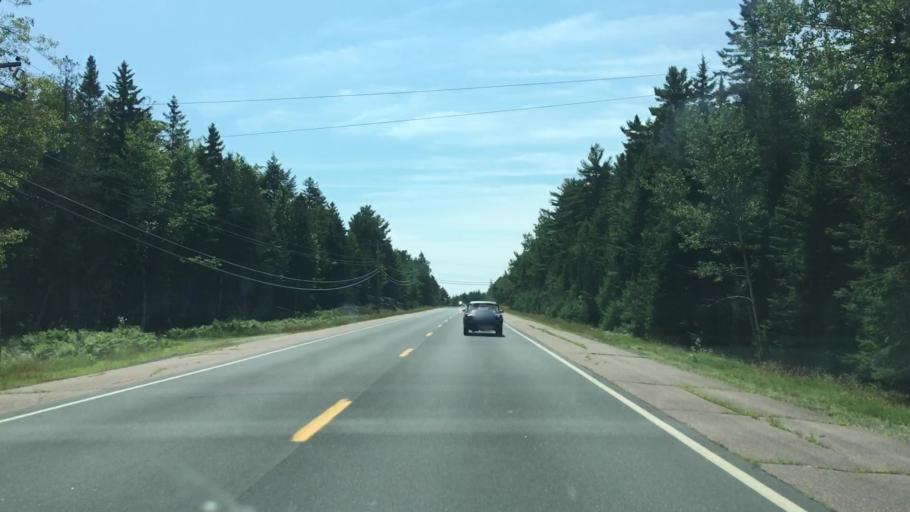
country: US
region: Maine
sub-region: Washington County
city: Calais
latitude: 45.1450
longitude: -67.1668
